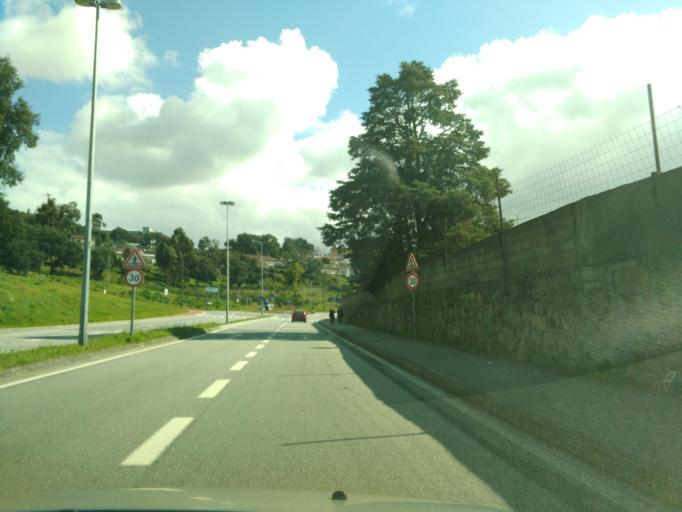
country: PT
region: Braga
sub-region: Braga
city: Braga
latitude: 41.5396
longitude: -8.4188
